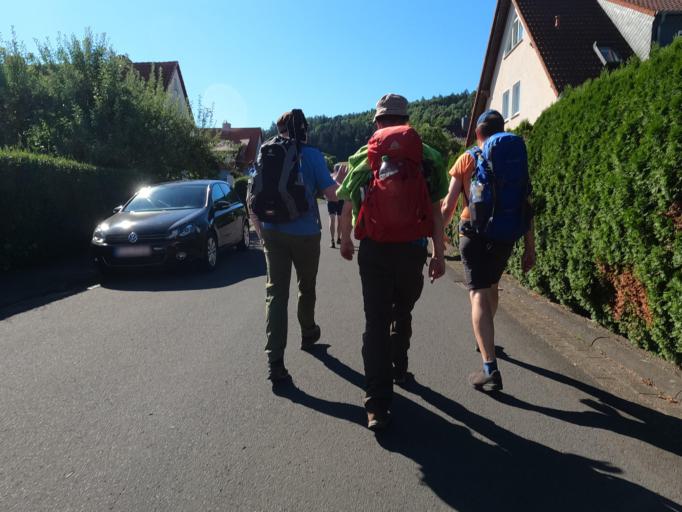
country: DE
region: Hesse
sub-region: Regierungsbezirk Darmstadt
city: Schluchtern
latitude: 50.3439
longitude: 9.5317
